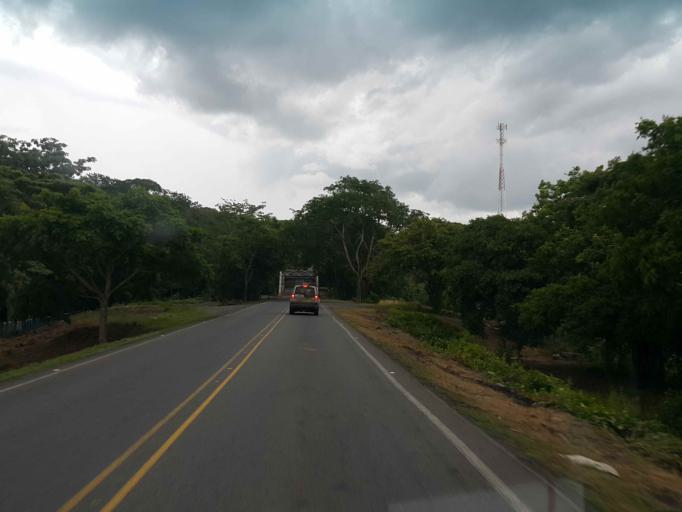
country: CR
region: Puntarenas
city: Miramar
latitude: 10.0708
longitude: -84.7728
